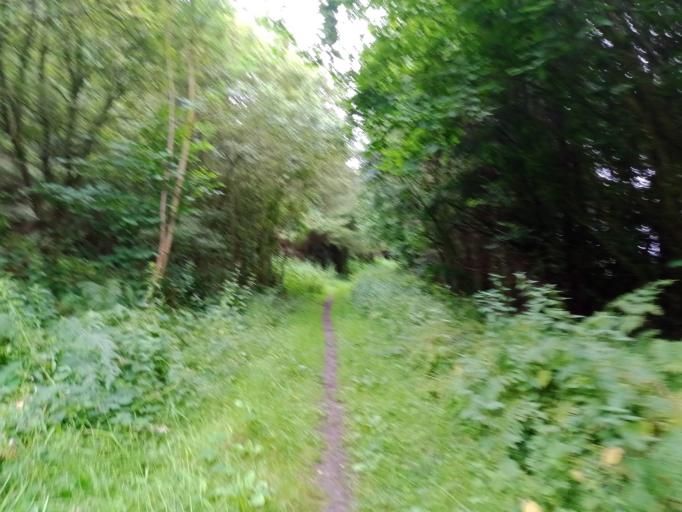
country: IE
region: Leinster
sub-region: Kilkenny
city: Ballyragget
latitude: 52.8228
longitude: -7.4072
